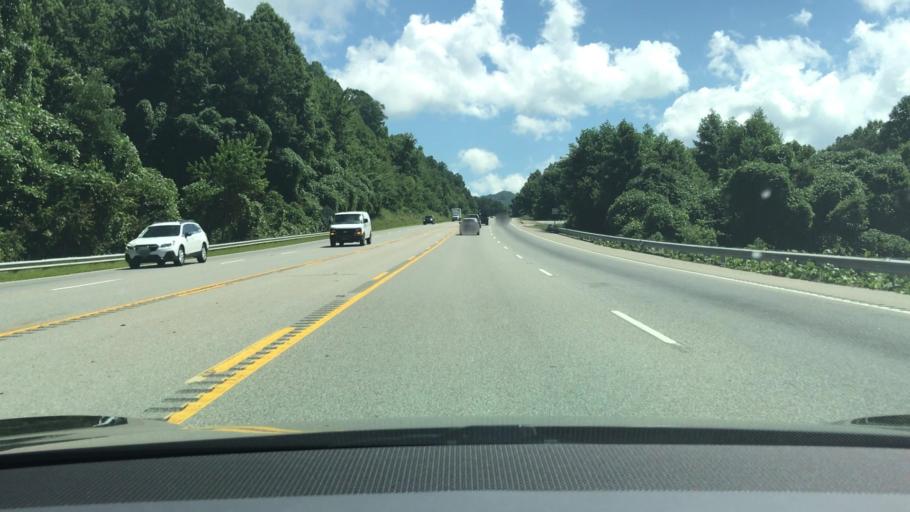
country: US
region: North Carolina
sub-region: Macon County
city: Franklin
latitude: 35.2402
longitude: -83.3286
